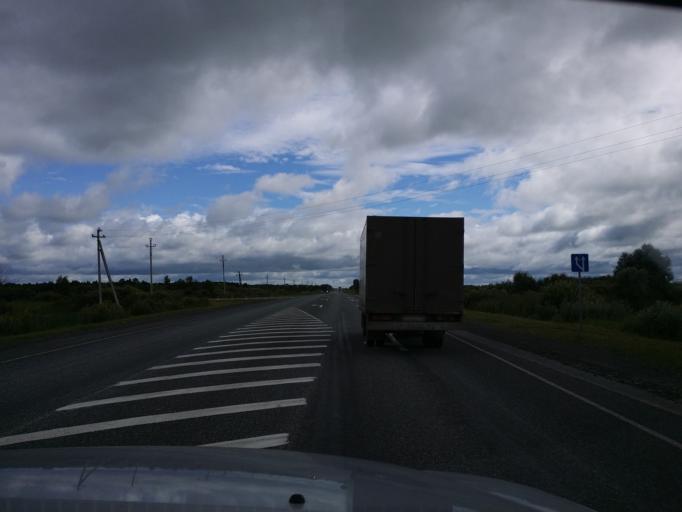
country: RU
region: Tjumen
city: Yarkovo
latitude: 57.2690
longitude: 66.8515
